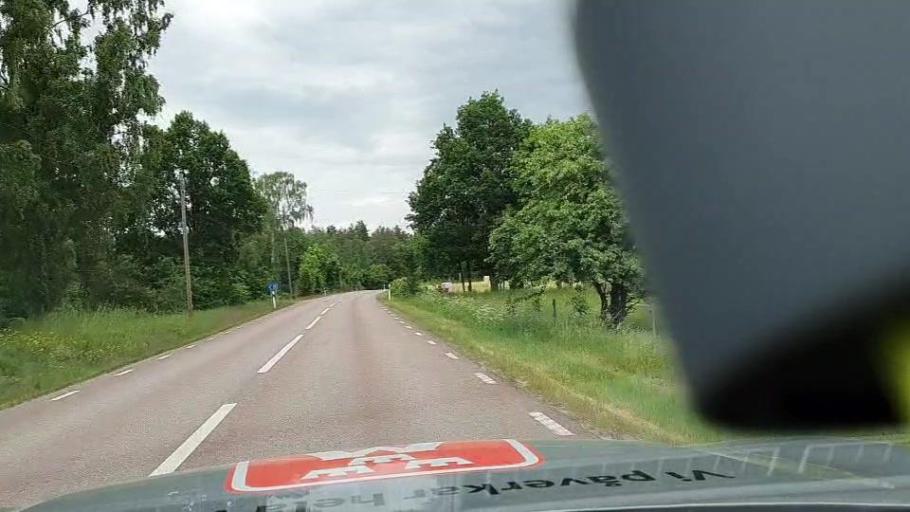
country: SE
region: Kalmar
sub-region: Emmaboda Kommun
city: Emmaboda
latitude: 56.4676
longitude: 15.5939
